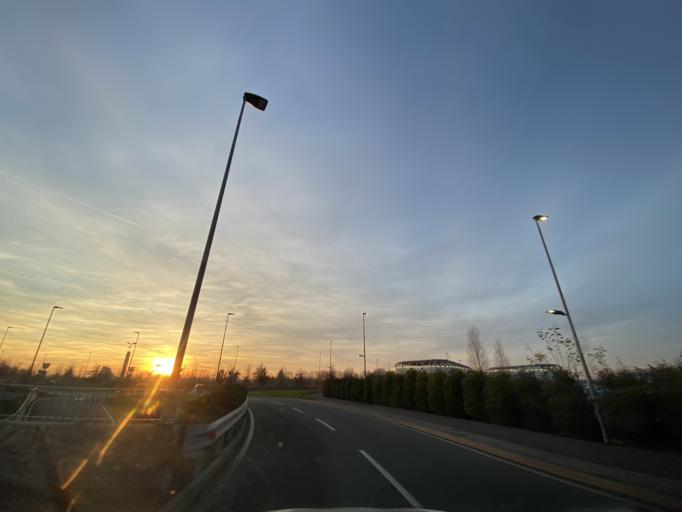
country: IT
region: Lombardy
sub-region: Citta metropolitana di Milano
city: Passirana
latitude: 45.5637
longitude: 9.0483
